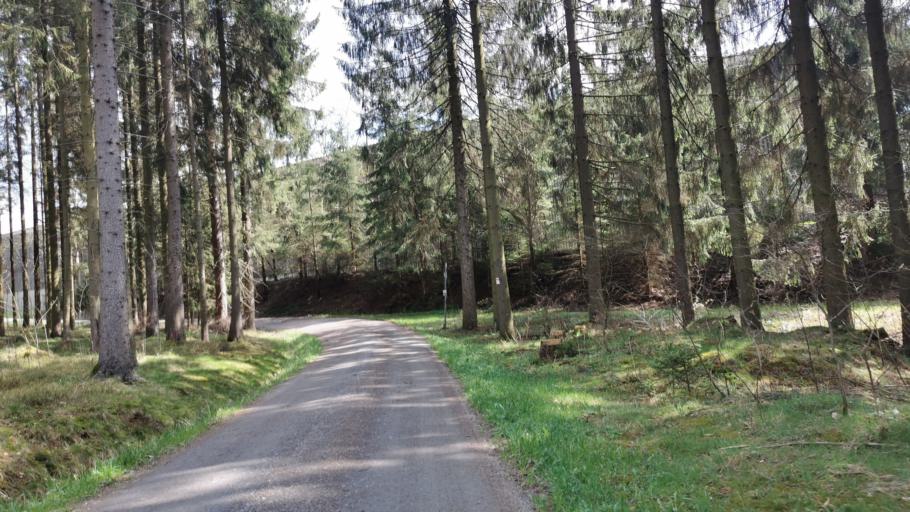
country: DE
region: Bavaria
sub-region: Upper Franconia
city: Teuschnitz
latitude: 50.4362
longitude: 11.3761
